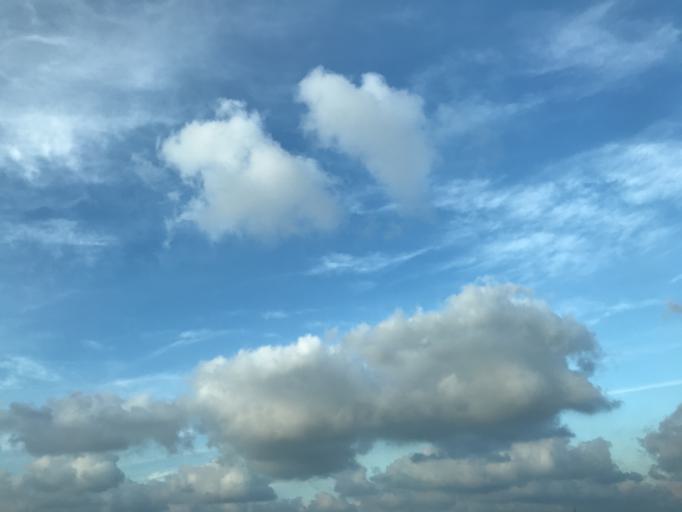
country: TR
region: Istanbul
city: Durusu
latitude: 41.2600
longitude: 28.7130
